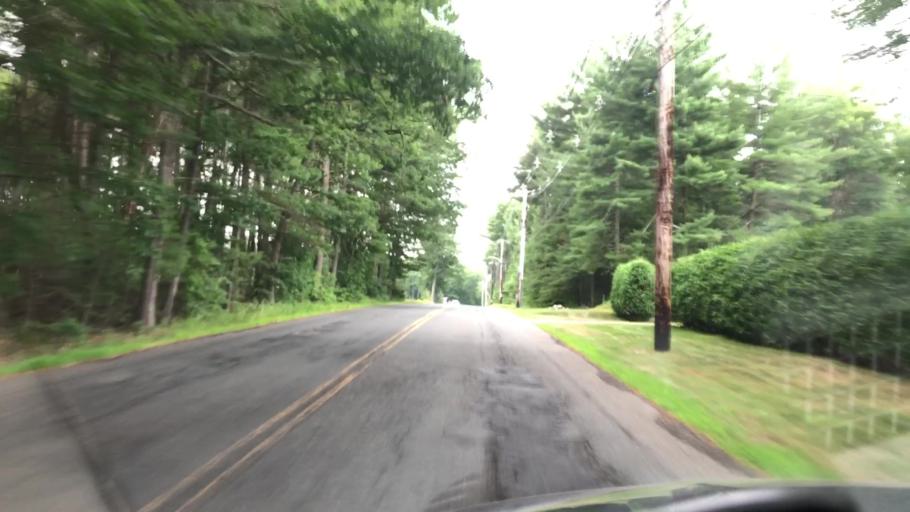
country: US
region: Massachusetts
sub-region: Hampden County
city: Westfield
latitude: 42.1777
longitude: -72.7493
